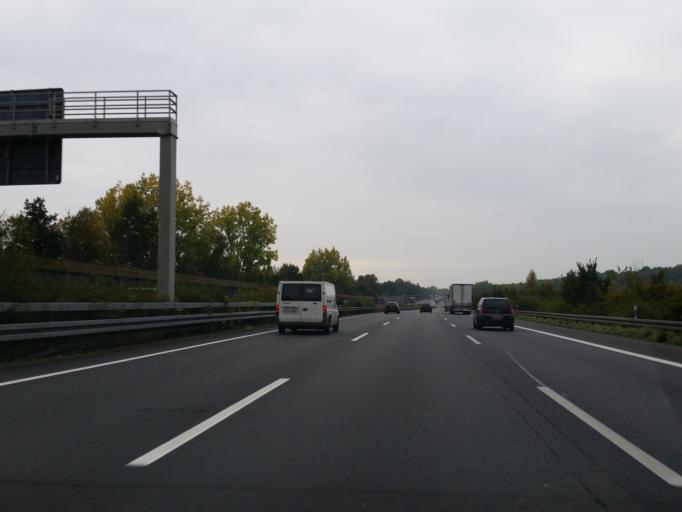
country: DE
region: Lower Saxony
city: Peine
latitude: 52.3403
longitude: 10.2237
